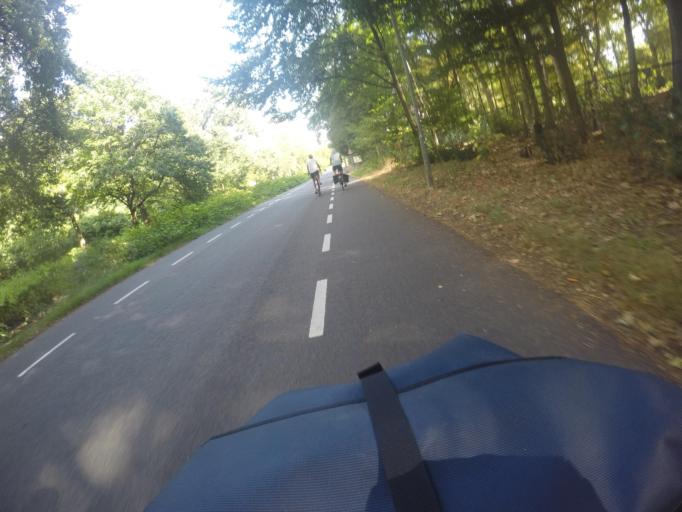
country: NL
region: Gelderland
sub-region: Gemeente Renkum
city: Oosterbeek
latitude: 51.9972
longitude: 5.8329
